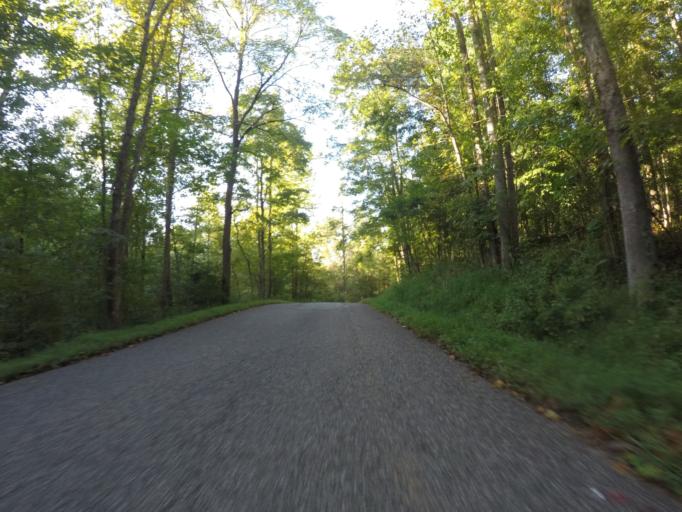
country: US
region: Kentucky
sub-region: Boyd County
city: Ashland
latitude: 38.5306
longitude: -82.5337
